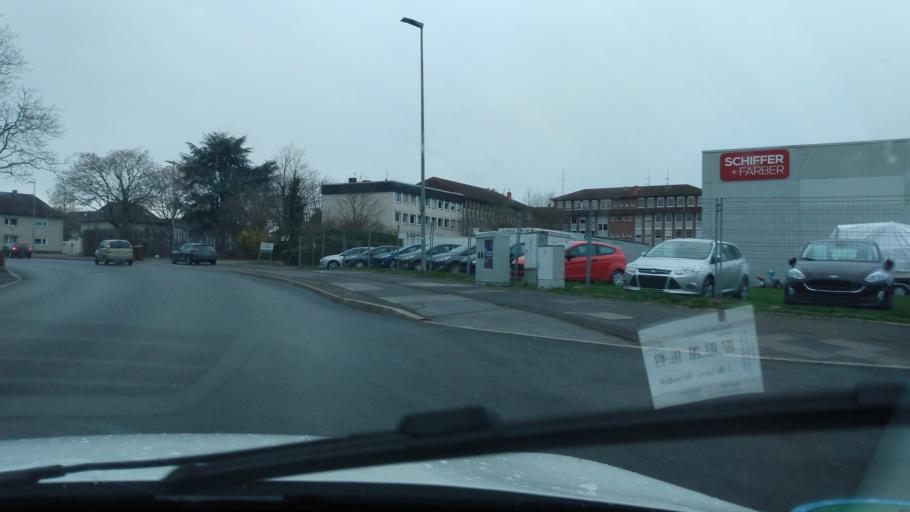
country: DE
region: North Rhine-Westphalia
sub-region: Regierungsbezirk Koln
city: Hurth
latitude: 50.8820
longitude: 6.8983
